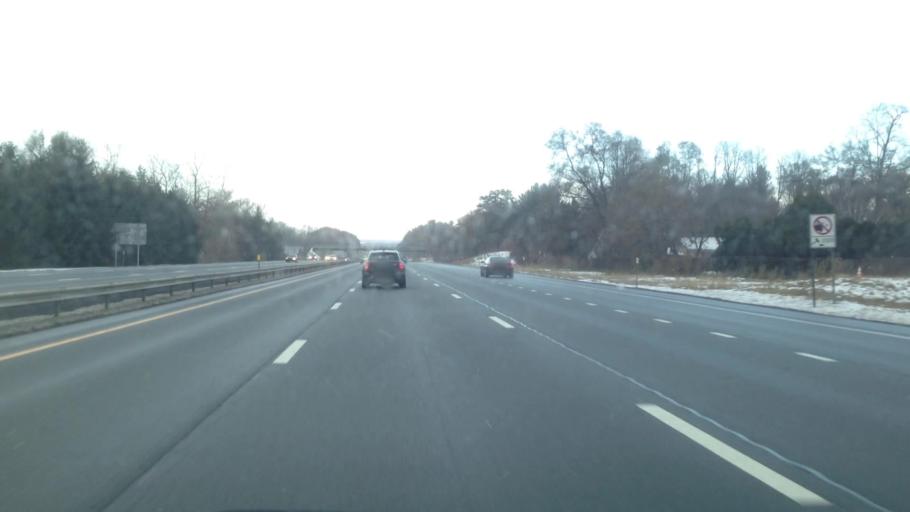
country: US
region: New York
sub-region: Schenectady County
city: Rotterdam
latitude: 42.7564
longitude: -73.9383
